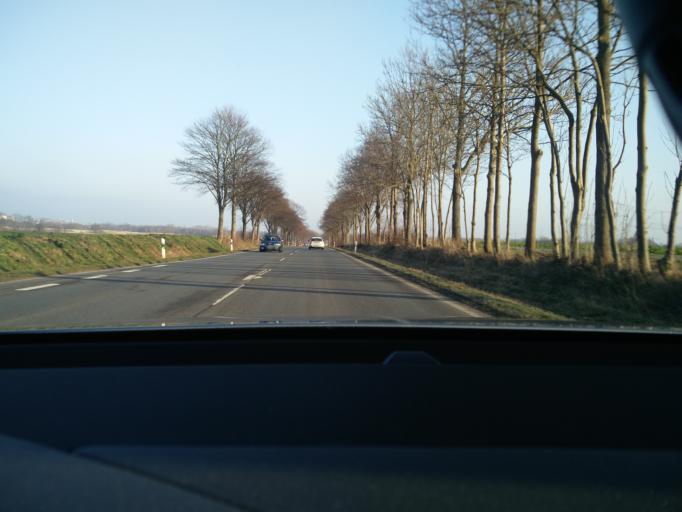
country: DE
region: Lower Saxony
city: Ilsede
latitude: 52.3040
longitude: 10.1922
